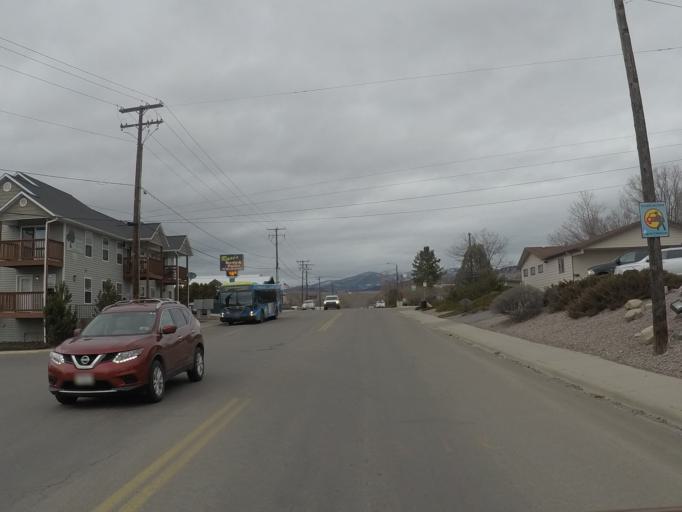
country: US
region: Montana
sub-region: Missoula County
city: Missoula
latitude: 46.8813
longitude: -114.0185
